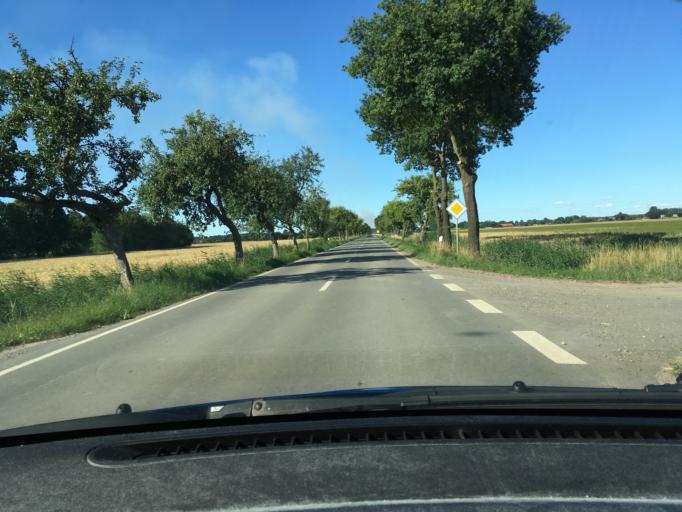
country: DE
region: Mecklenburg-Vorpommern
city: Boizenburg
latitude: 53.3435
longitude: 10.6942
